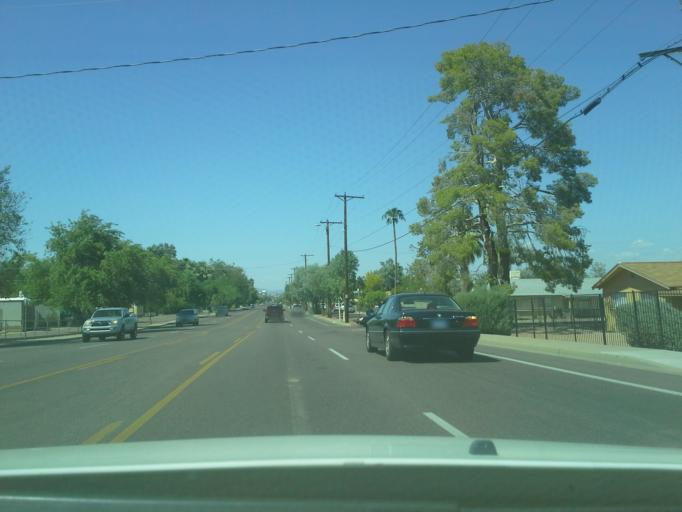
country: US
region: Arizona
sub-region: Maricopa County
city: Phoenix
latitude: 33.3800
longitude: -112.0646
